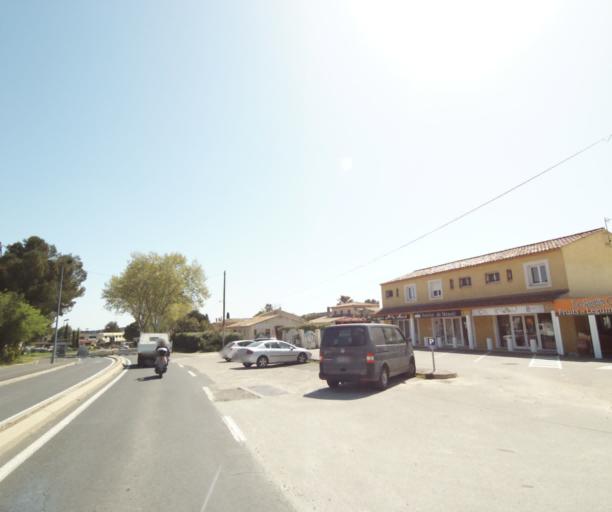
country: FR
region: Languedoc-Roussillon
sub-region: Departement de l'Herault
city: Clapiers
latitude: 43.6600
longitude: 3.8975
